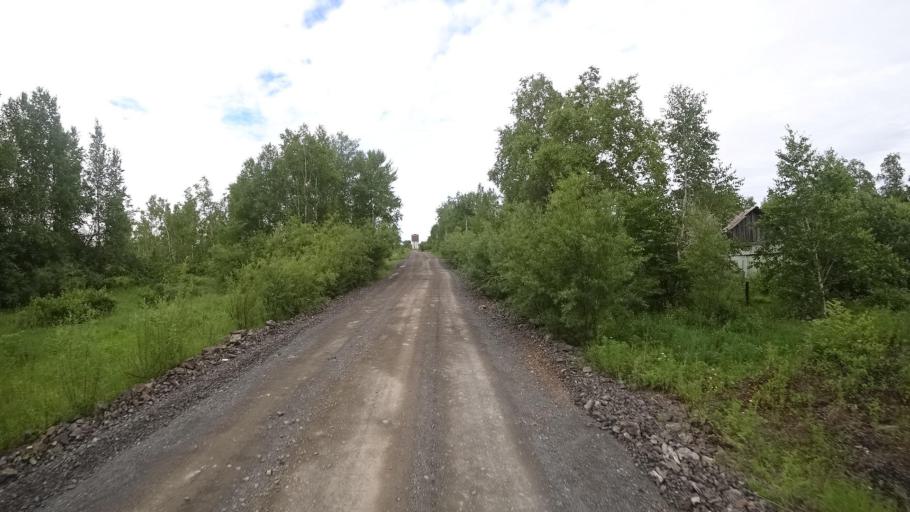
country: RU
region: Khabarovsk Krai
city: Amursk
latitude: 49.9037
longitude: 136.1383
